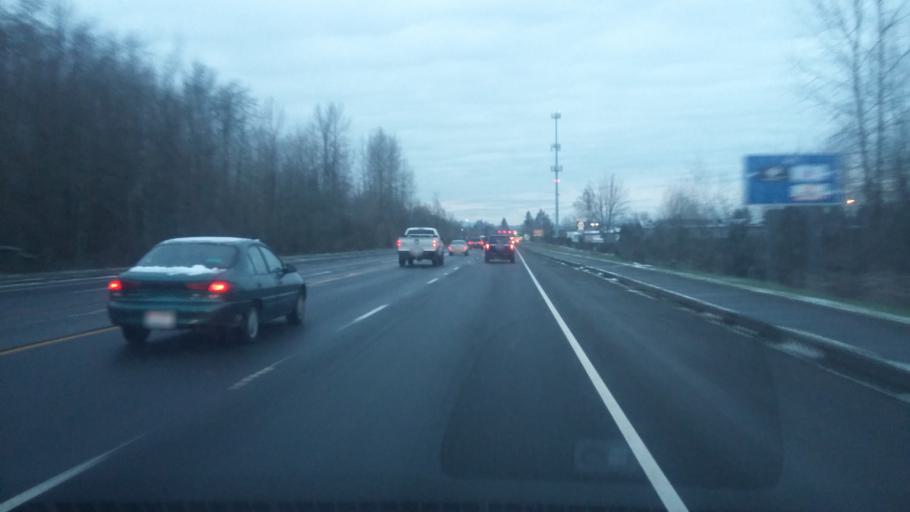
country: US
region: Washington
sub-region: Clark County
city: Battle Ground
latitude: 45.7756
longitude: -122.5474
